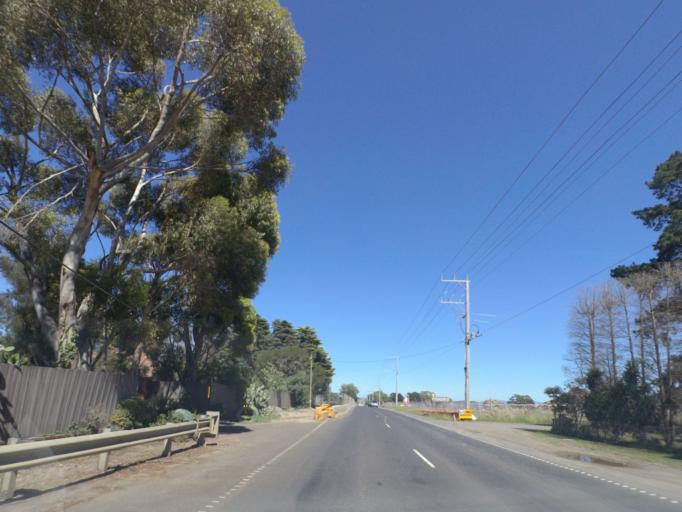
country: AU
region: Victoria
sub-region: Hume
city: Craigieburn
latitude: -37.5437
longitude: 144.9798
